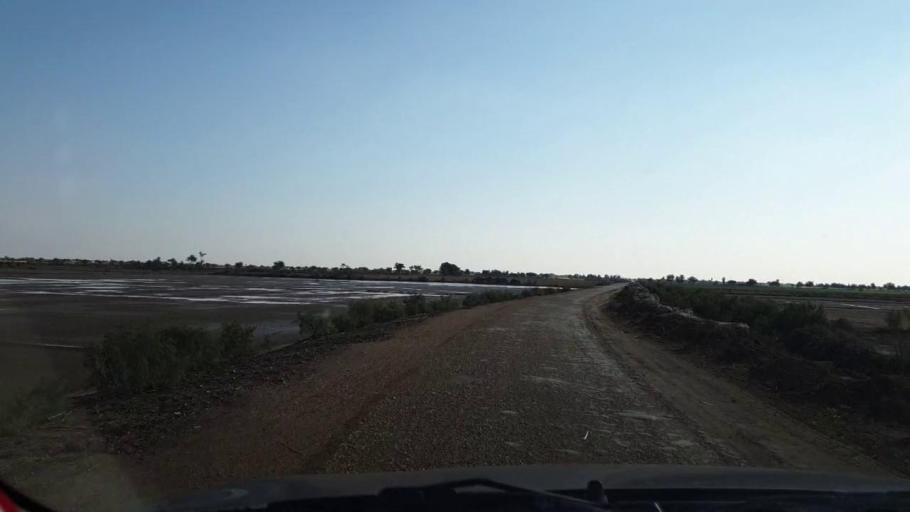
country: PK
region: Sindh
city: Sinjhoro
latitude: 26.0045
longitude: 68.8394
